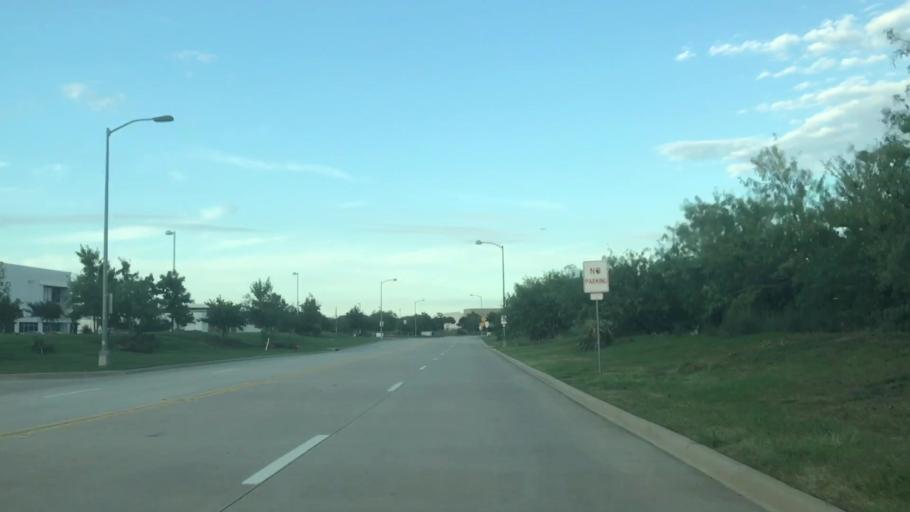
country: US
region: Texas
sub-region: Dallas County
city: Coppell
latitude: 32.9419
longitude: -97.0348
